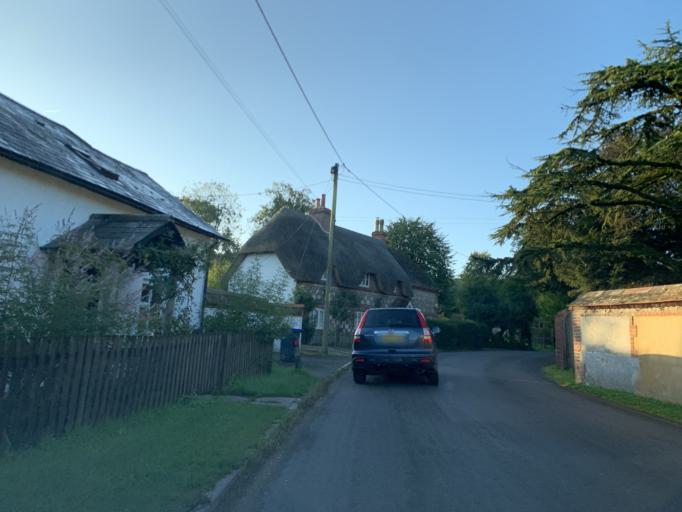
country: GB
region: England
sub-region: Wiltshire
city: Woodford
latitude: 51.1159
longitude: -1.8215
